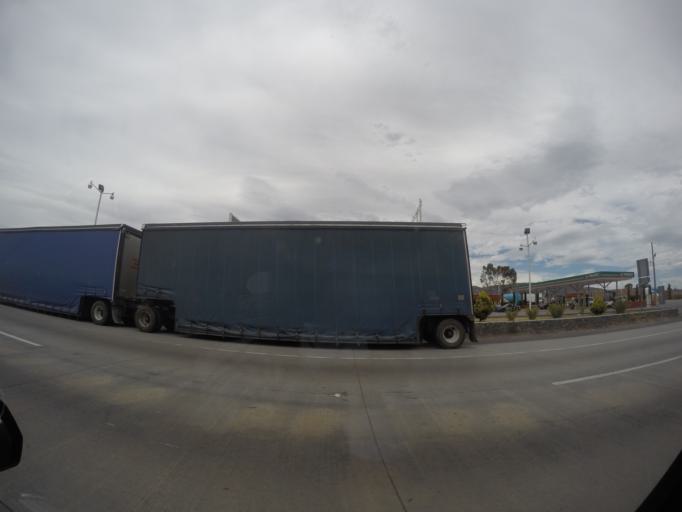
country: MX
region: Hidalgo
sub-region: Tepeji del Rio de Ocampo
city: Santiago Tlautla
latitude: 19.9843
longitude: -99.4397
